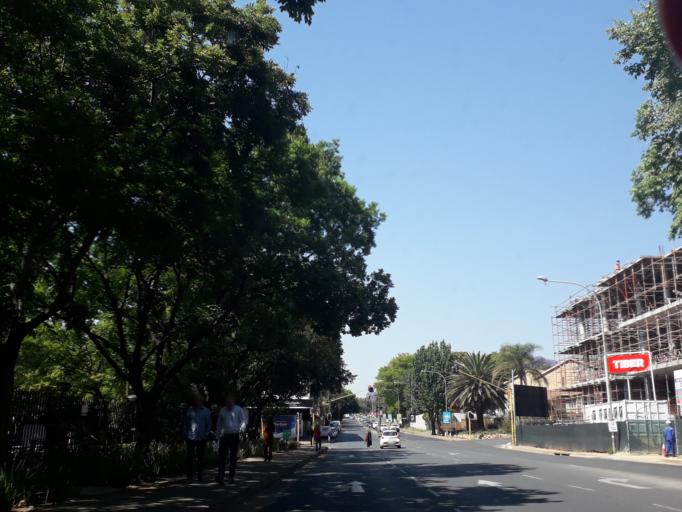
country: ZA
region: Gauteng
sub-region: City of Johannesburg Metropolitan Municipality
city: Johannesburg
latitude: -26.1308
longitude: 28.0492
